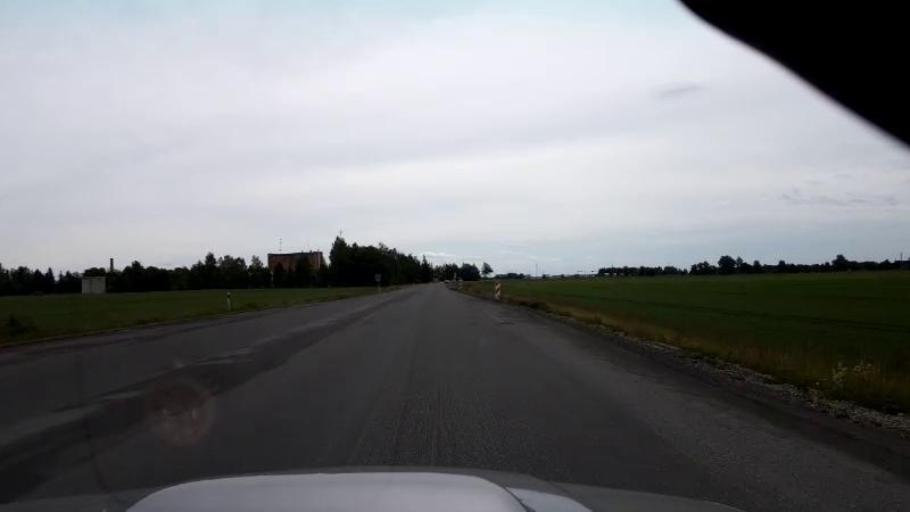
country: LV
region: Bauskas Rajons
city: Bauska
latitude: 56.3112
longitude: 24.3357
